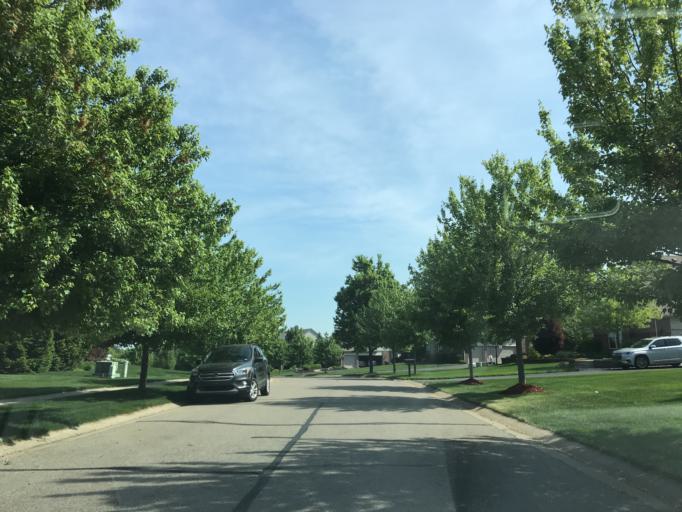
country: US
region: Michigan
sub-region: Oakland County
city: South Lyon
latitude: 42.4784
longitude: -83.6339
